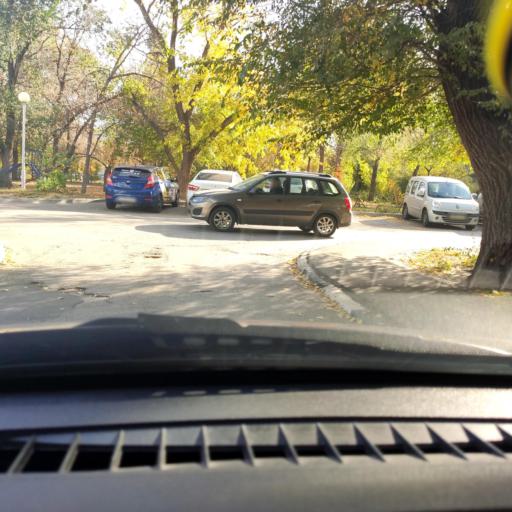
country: RU
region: Samara
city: Tol'yatti
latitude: 53.5352
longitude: 49.2898
